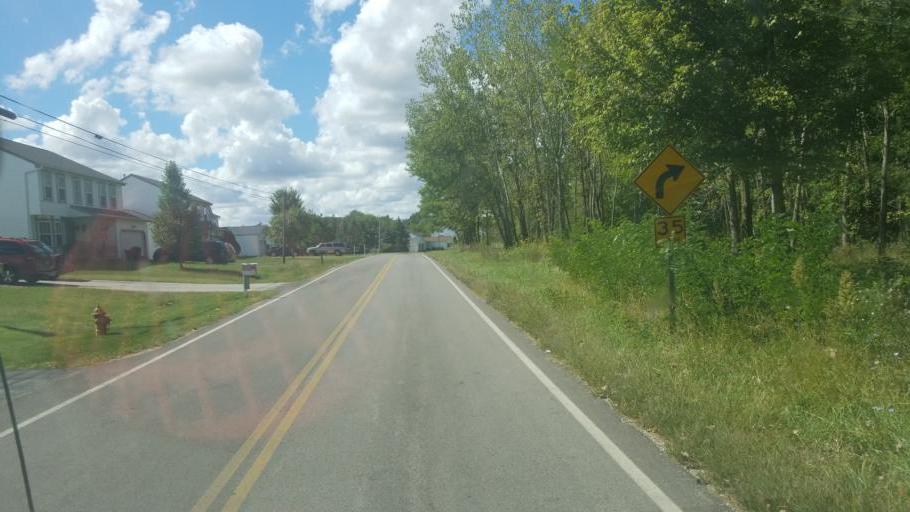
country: US
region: Ohio
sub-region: Union County
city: Marysville
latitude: 40.1811
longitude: -83.4443
